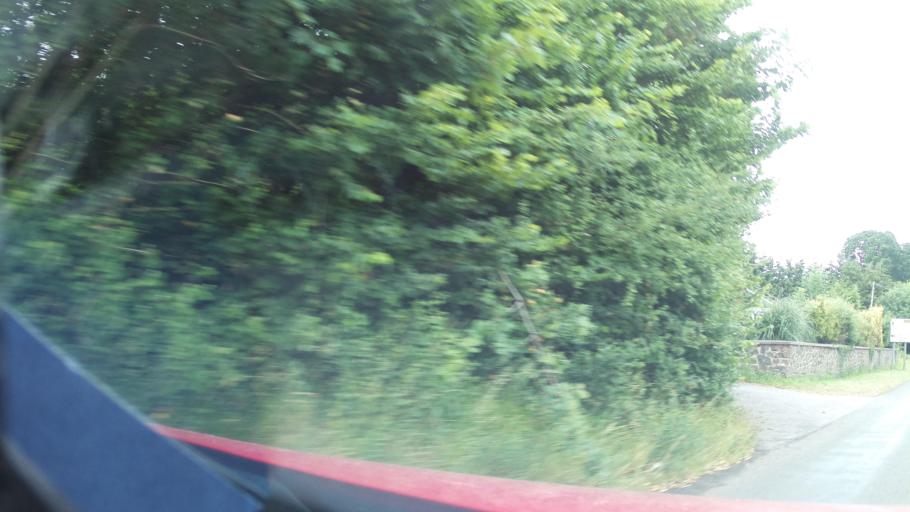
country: GB
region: England
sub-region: Devon
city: Newton Poppleford
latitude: 50.7546
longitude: -3.3431
